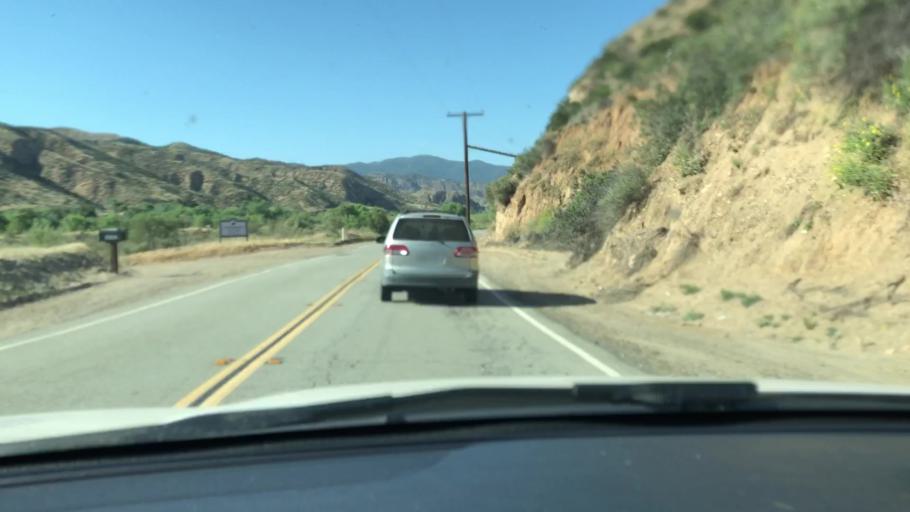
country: US
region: California
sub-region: Los Angeles County
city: Castaic
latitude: 34.5019
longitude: -118.5396
